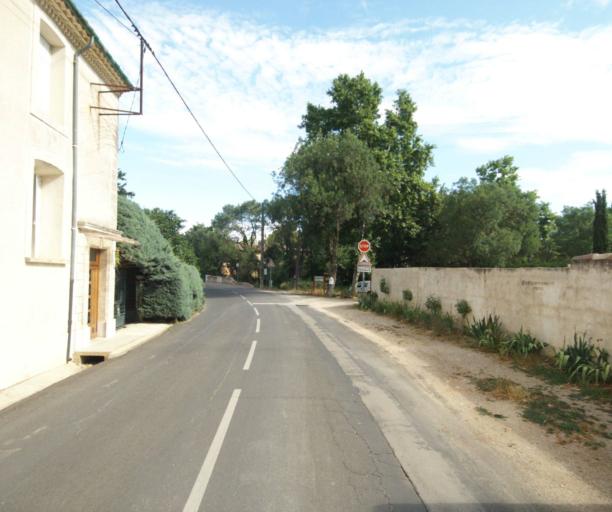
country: FR
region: Languedoc-Roussillon
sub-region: Departement de l'Herault
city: Aniane
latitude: 43.6843
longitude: 3.5942
